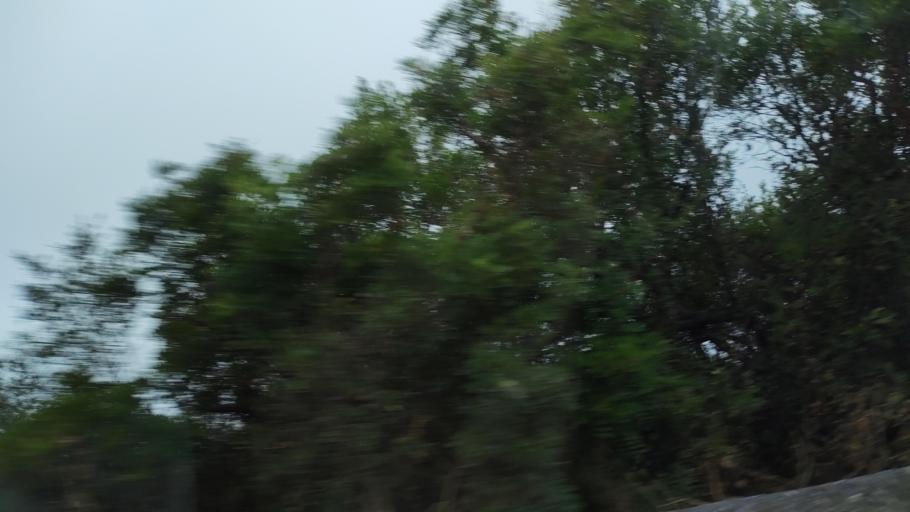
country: GI
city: Gibraltar
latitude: 36.1310
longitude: -5.3475
